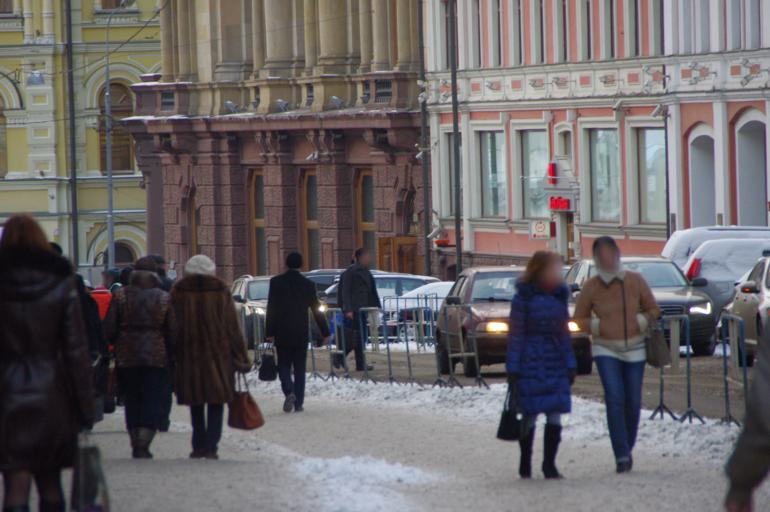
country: RU
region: Moscow
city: Moscow
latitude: 55.7616
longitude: 37.6269
